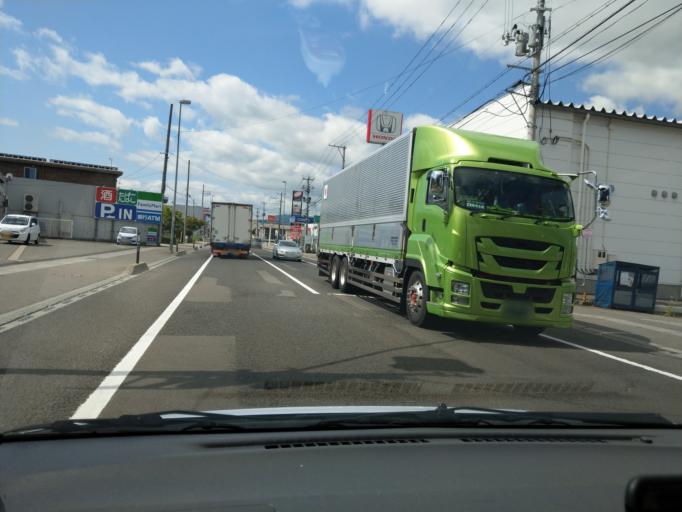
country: JP
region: Akita
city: Yuzawa
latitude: 39.1761
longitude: 140.4925
